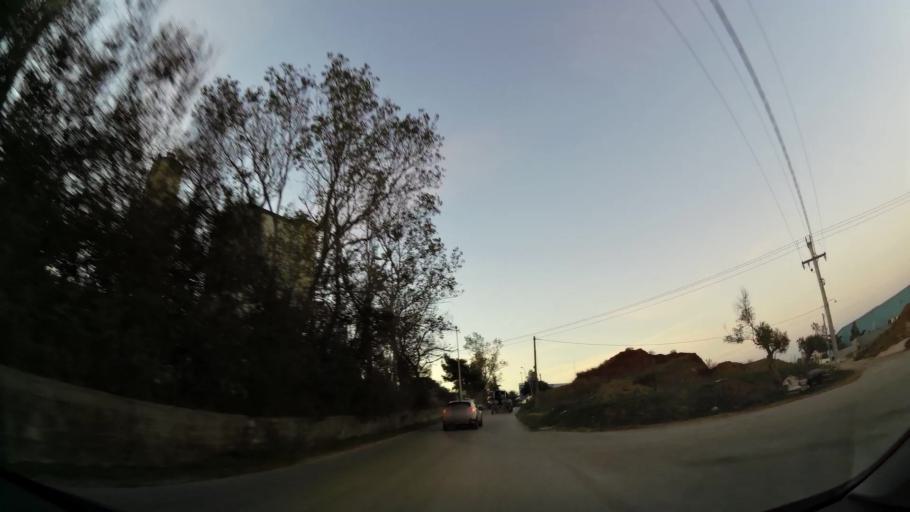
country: GR
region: Attica
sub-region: Nomarchia Anatolikis Attikis
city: Pikermi
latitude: 38.0083
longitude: 23.9729
